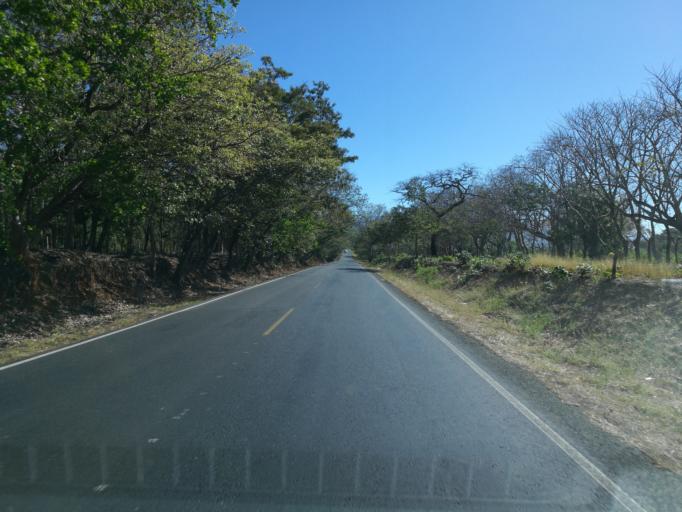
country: CR
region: Puntarenas
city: Miramar
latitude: 10.0904
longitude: -84.8289
